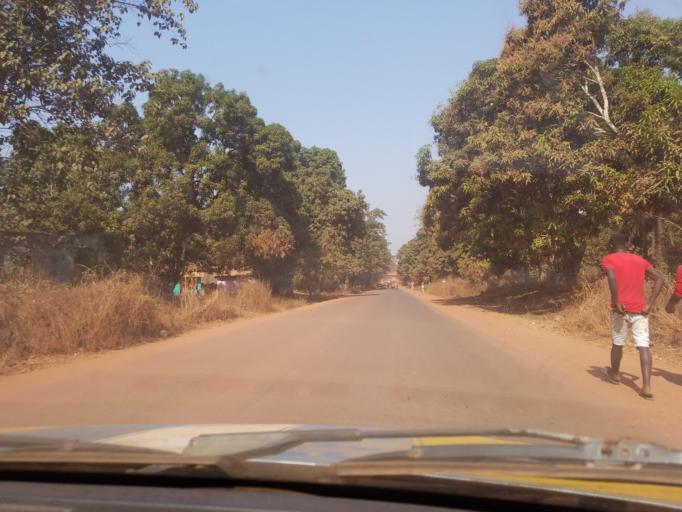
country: GN
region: Boke
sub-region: Boke Prefecture
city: Sangueya
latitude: 10.8080
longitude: -14.3867
